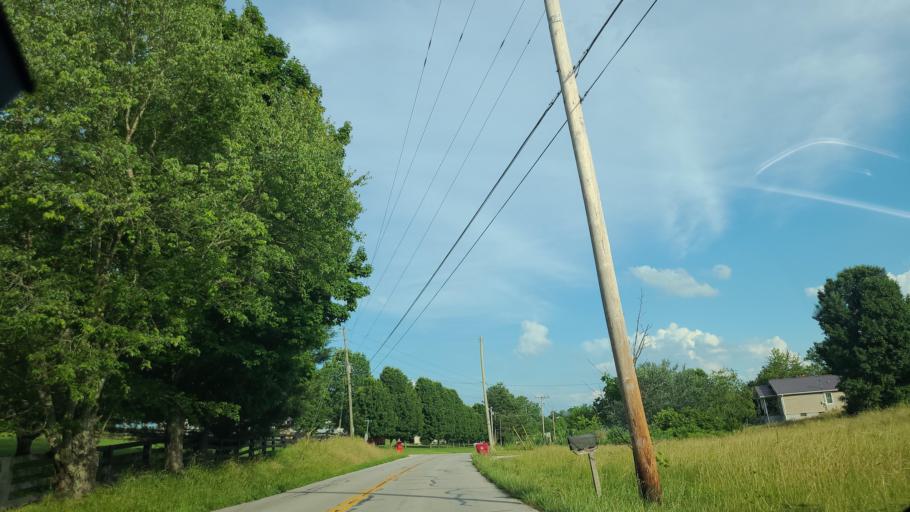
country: US
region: Kentucky
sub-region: Whitley County
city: Corbin
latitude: 36.9045
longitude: -84.2385
